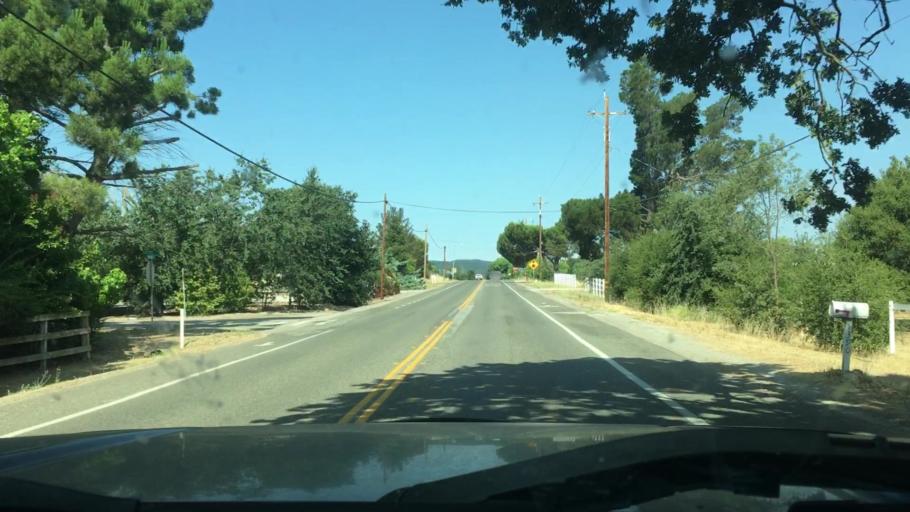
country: US
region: California
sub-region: San Luis Obispo County
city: Templeton
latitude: 35.5433
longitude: -120.7285
